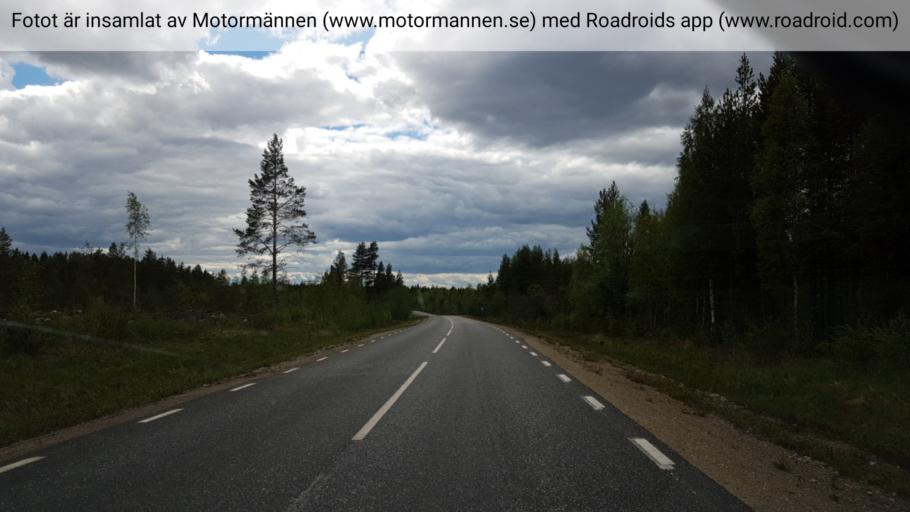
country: SE
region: Vaesterbotten
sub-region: Vindelns Kommun
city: Vindeln
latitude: 64.5376
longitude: 19.8994
